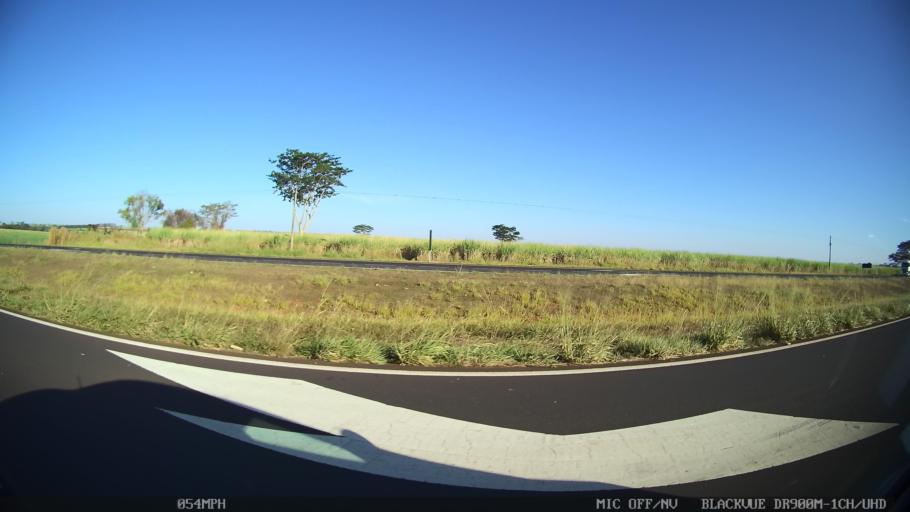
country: BR
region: Sao Paulo
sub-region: Olimpia
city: Olimpia
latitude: -20.7236
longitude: -49.0275
